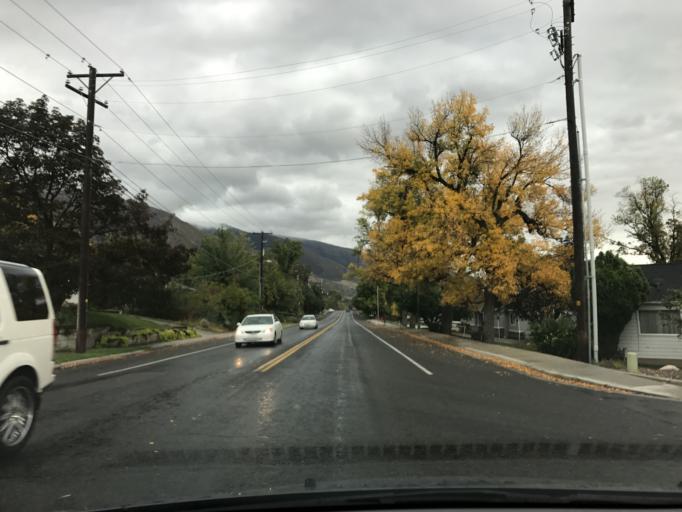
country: US
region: Utah
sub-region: Davis County
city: Fruit Heights
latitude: 41.0060
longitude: -111.9058
